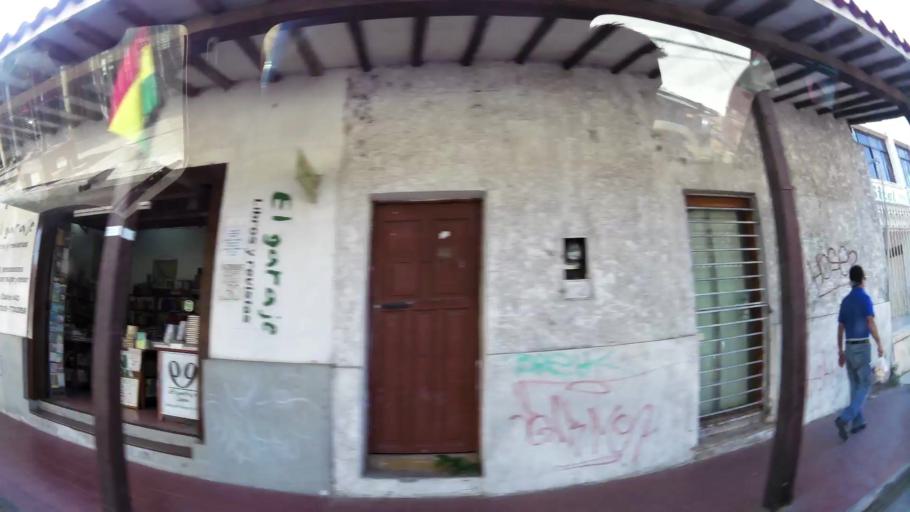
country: BO
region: Santa Cruz
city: Santa Cruz de la Sierra
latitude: -17.7851
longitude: -63.1764
